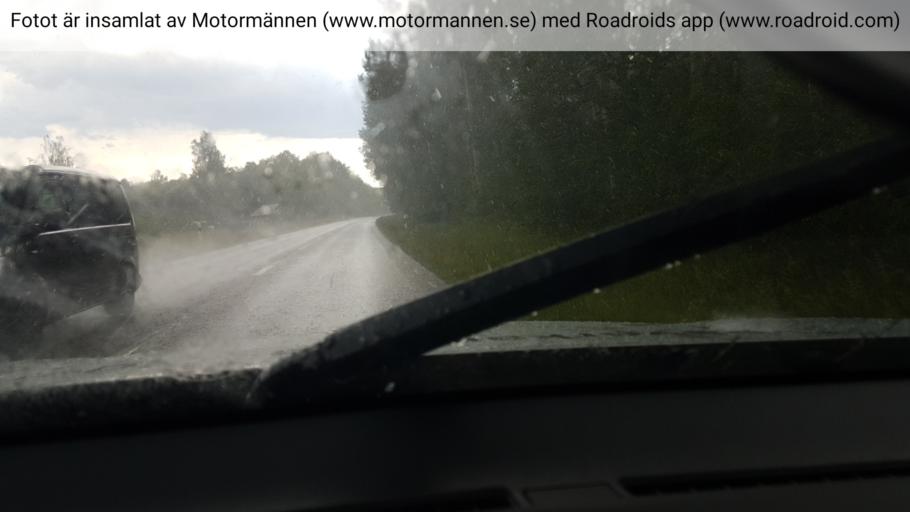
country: SE
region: Vaestra Goetaland
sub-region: Hjo Kommun
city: Hjo
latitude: 58.2390
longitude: 14.2256
